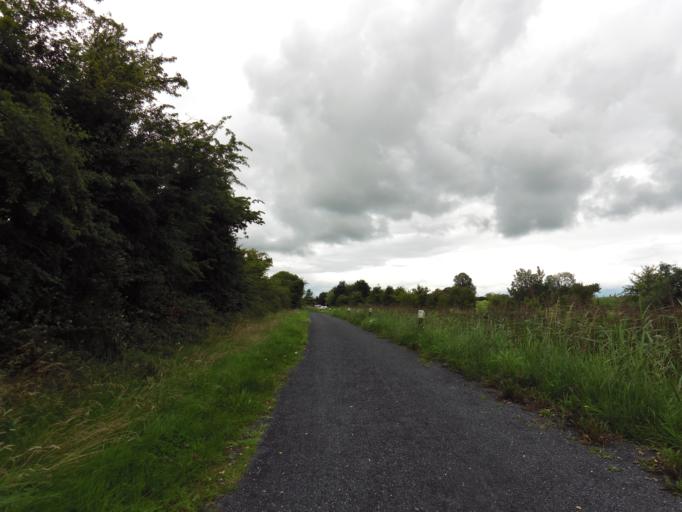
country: IE
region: Leinster
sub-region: An Iarmhi
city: An Muileann gCearr
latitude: 53.5334
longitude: -7.4649
